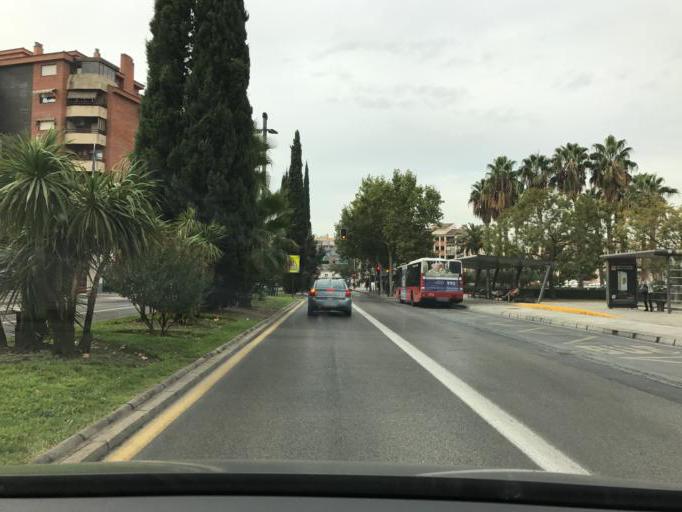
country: ES
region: Andalusia
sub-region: Provincia de Granada
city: Granada
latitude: 37.1655
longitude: -3.5992
